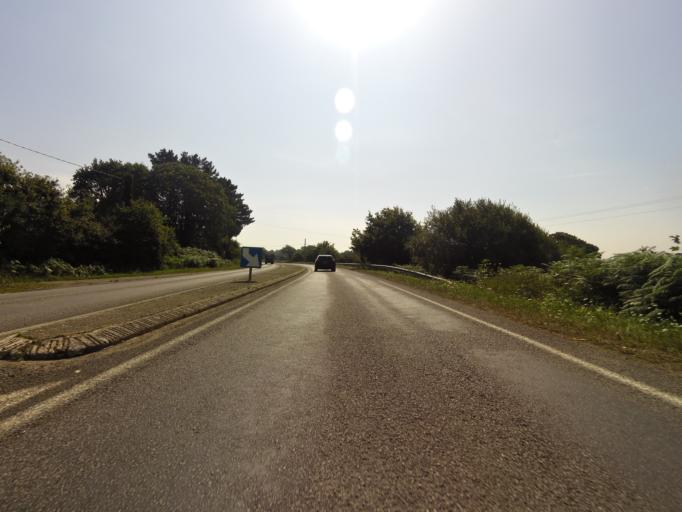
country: FR
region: Brittany
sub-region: Departement du Finistere
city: Plogastel-Saint-Germain
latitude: 47.9970
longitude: -4.2570
